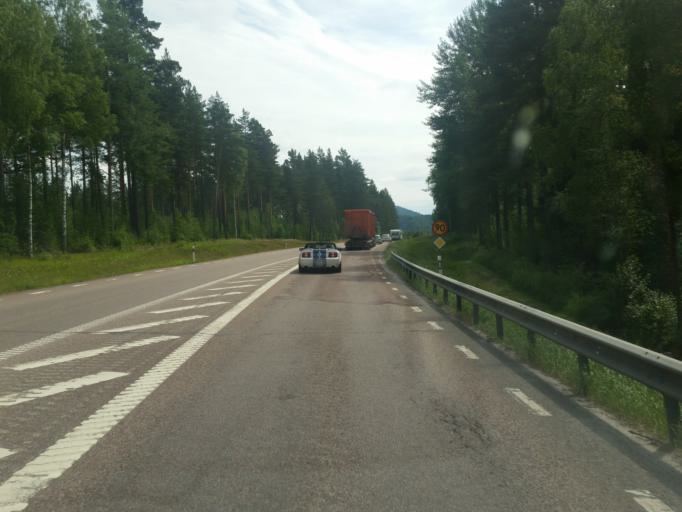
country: SE
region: Dalarna
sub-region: Gagnefs Kommun
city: Djuras
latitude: 60.5521
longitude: 15.2108
